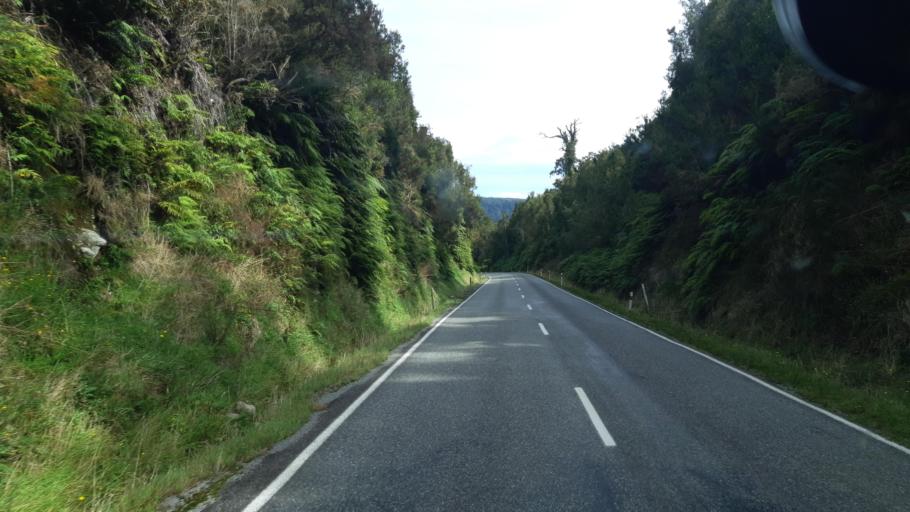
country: NZ
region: West Coast
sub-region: Westland District
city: Hokitika
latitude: -43.0411
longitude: 170.6422
